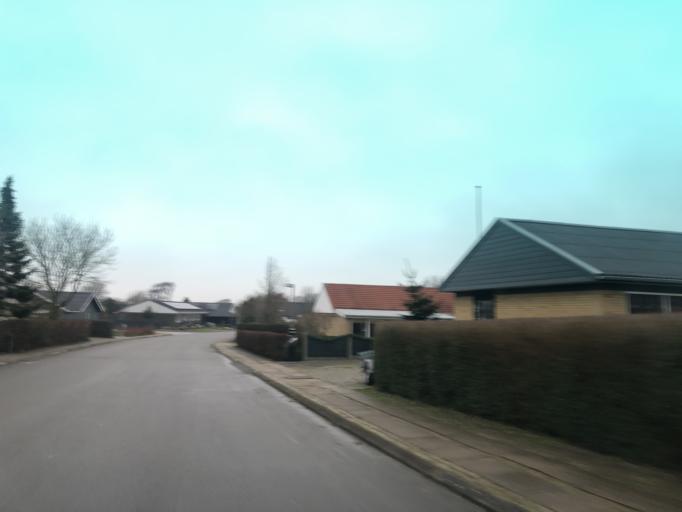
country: DK
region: North Denmark
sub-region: Thisted Kommune
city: Hurup
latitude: 56.7512
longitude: 8.4288
